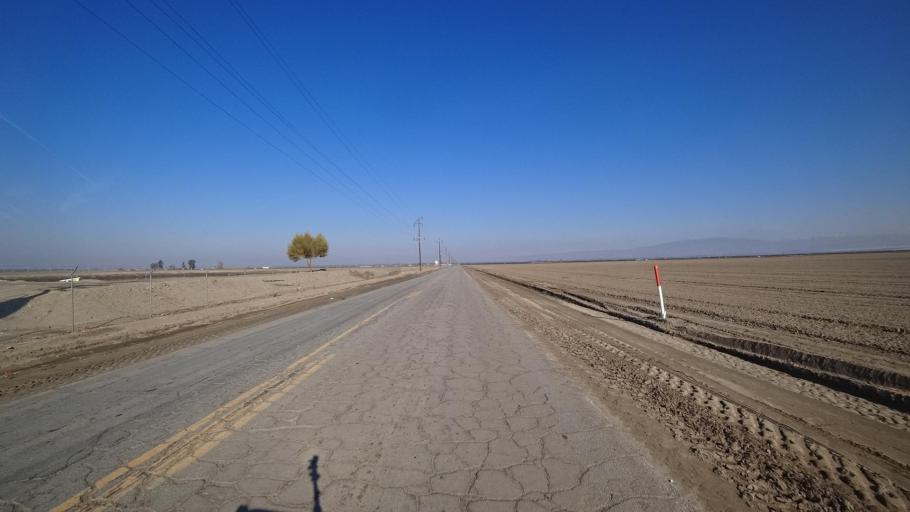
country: US
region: California
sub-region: Kern County
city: Arvin
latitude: 35.1515
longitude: -118.8781
